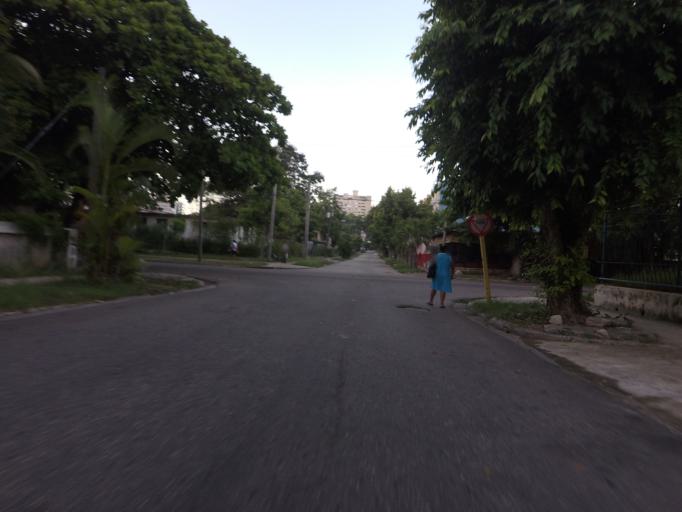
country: CU
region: La Habana
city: Cerro
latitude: 23.1163
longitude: -82.3936
